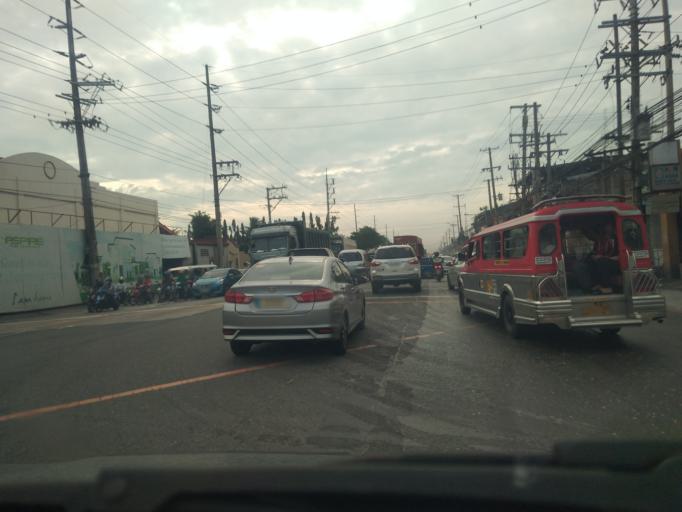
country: PH
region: Central Luzon
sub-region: Province of Pampanga
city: Bulaon
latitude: 15.0745
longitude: 120.6435
